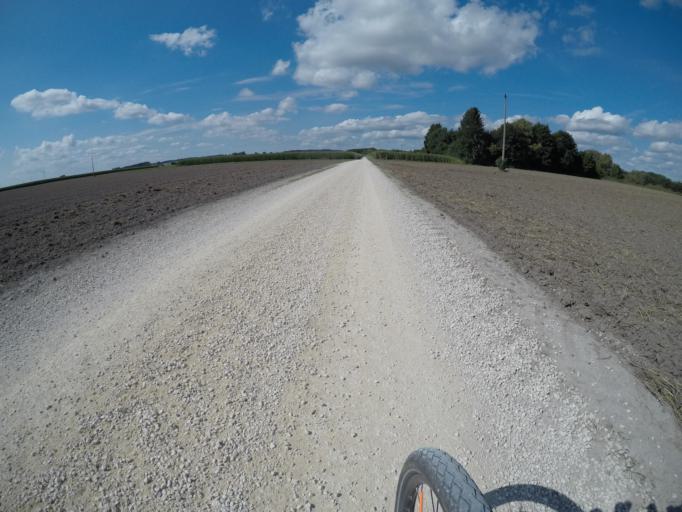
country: DE
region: Bavaria
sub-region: Swabia
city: Wittislingen
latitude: 48.6106
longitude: 10.4363
